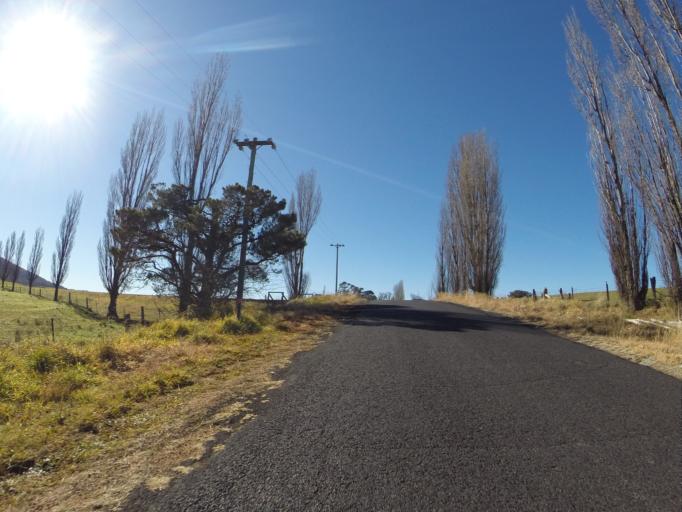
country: AU
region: New South Wales
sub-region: Oberon
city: Oberon
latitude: -33.5396
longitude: 149.8807
